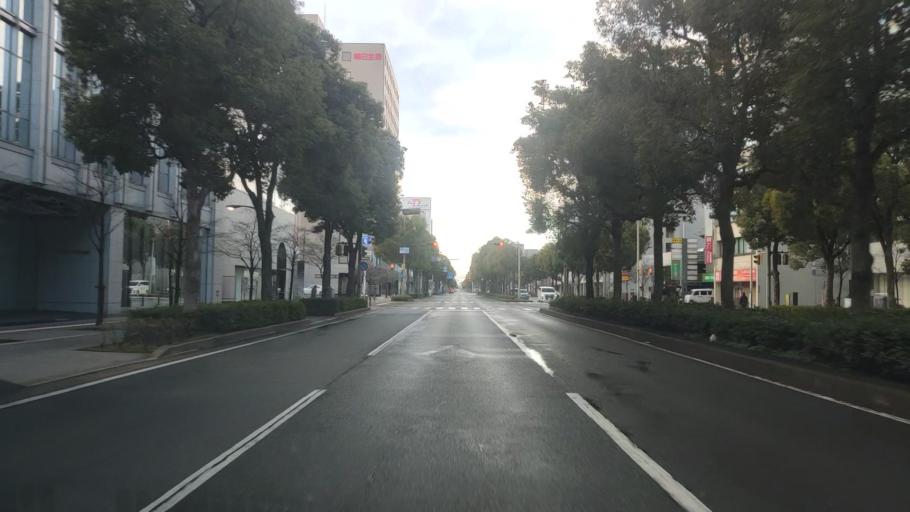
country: JP
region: Hyogo
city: Himeji
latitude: 34.8241
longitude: 134.6885
